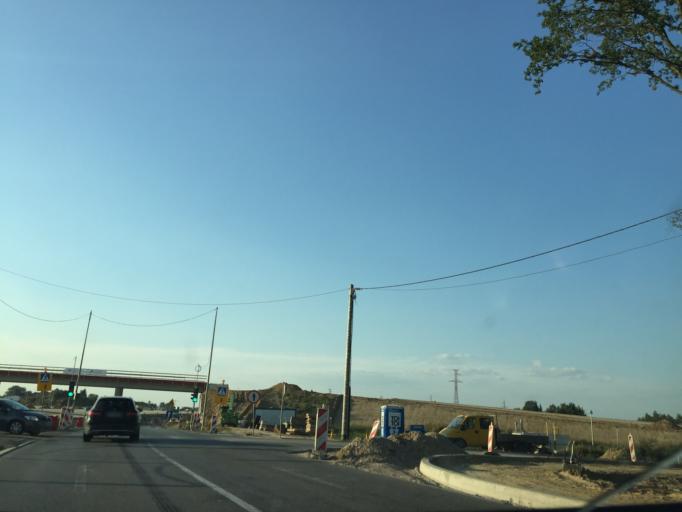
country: PL
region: Masovian Voivodeship
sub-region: Powiat piaseczynski
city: Tarczyn
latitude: 51.9435
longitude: 20.8452
